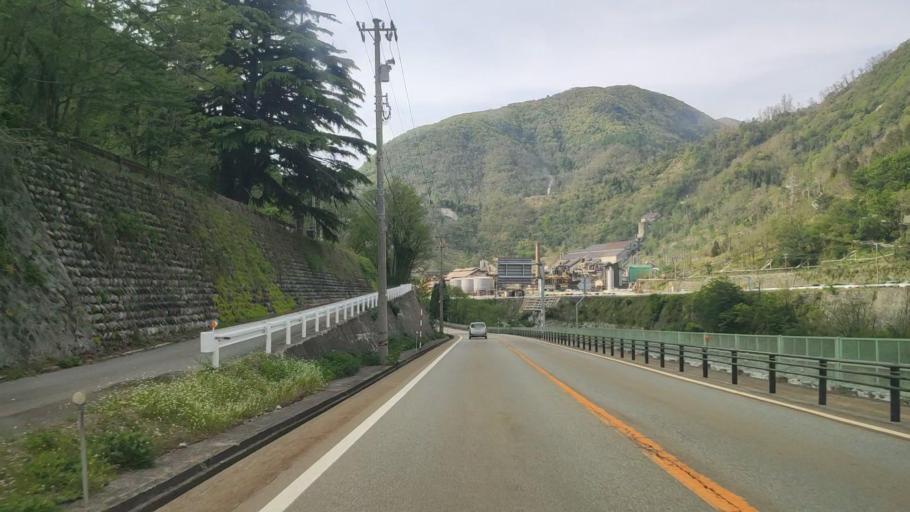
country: JP
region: Gifu
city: Takayama
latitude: 36.3428
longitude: 137.2949
